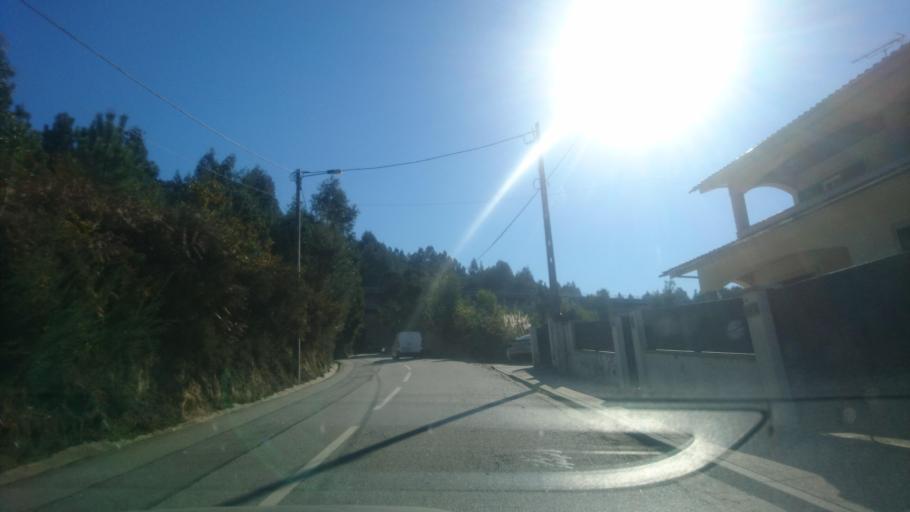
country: PT
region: Aveiro
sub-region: Oliveira de Azemeis
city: Vila Cha
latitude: 40.8671
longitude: -8.4397
